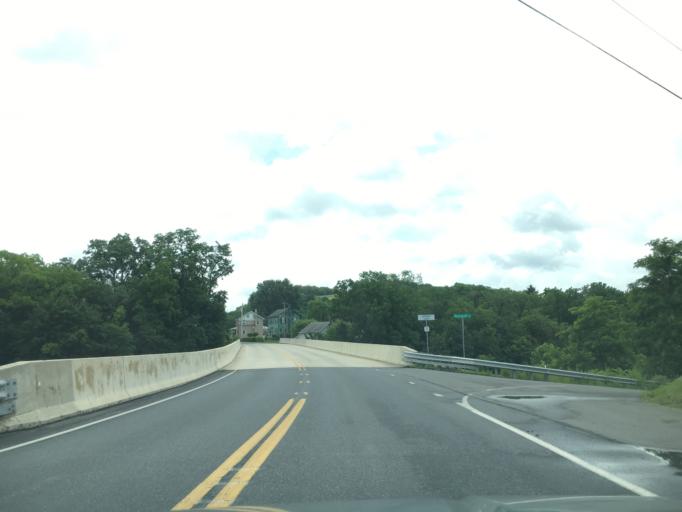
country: US
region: Pennsylvania
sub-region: Lehigh County
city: Cementon
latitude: 40.7016
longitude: -75.5172
